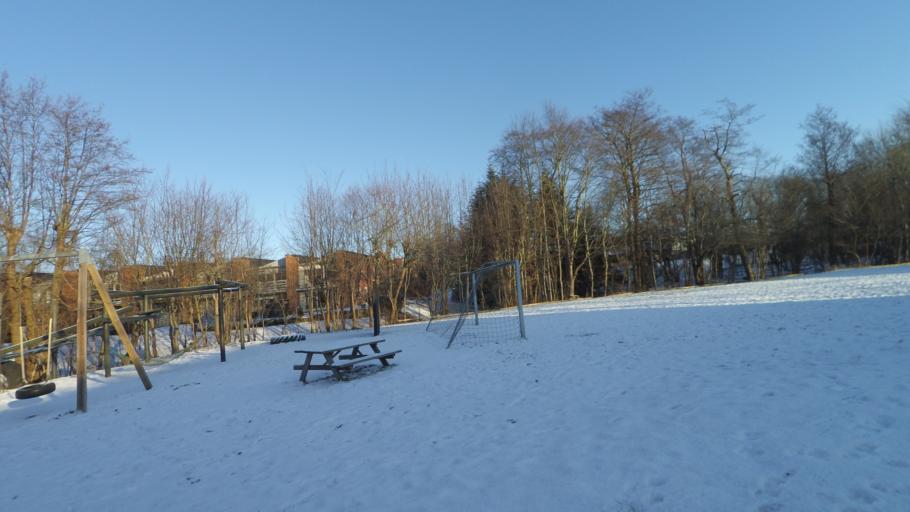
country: DK
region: Central Jutland
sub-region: Arhus Kommune
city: Stavtrup
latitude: 56.1517
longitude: 10.0883
